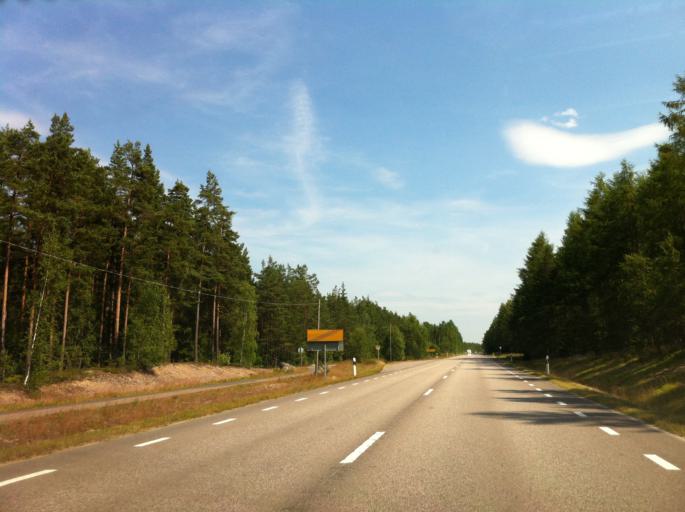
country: SE
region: Kalmar
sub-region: Nybro Kommun
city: Nybro
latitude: 56.8404
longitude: 15.7170
